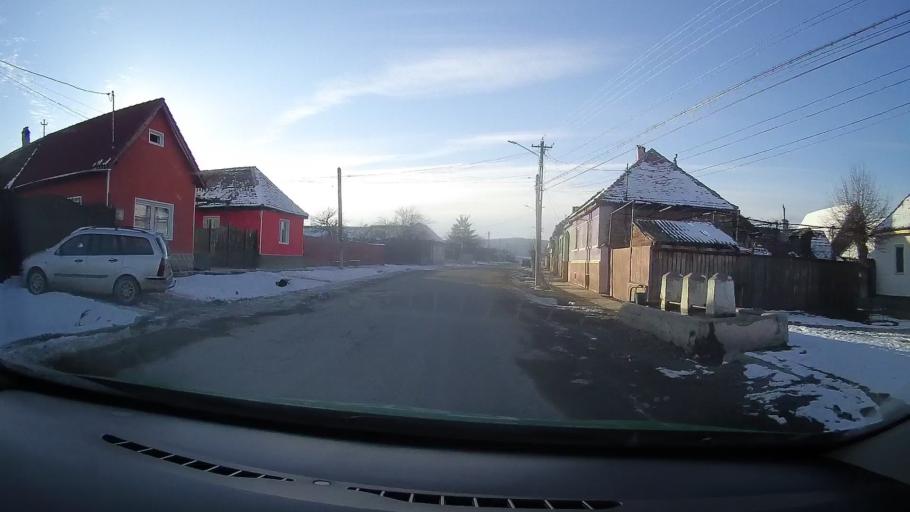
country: RO
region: Sibiu
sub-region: Comuna Merghindeal
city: Merghindeal
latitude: 45.9665
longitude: 24.7171
